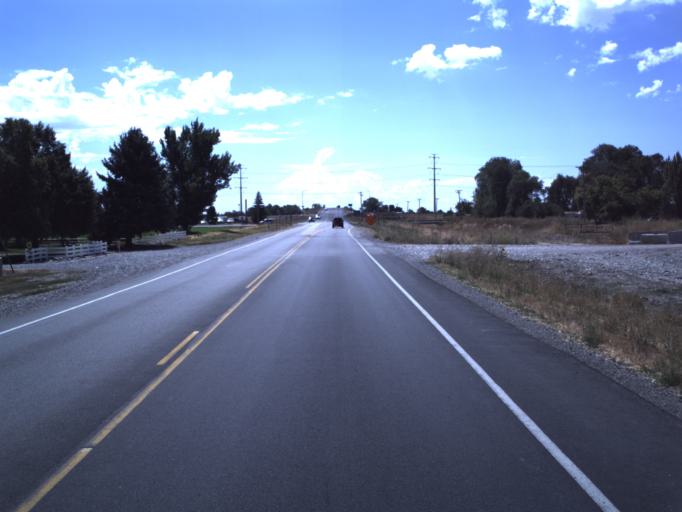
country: US
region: Utah
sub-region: Box Elder County
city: Elwood
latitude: 41.6859
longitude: -112.1414
